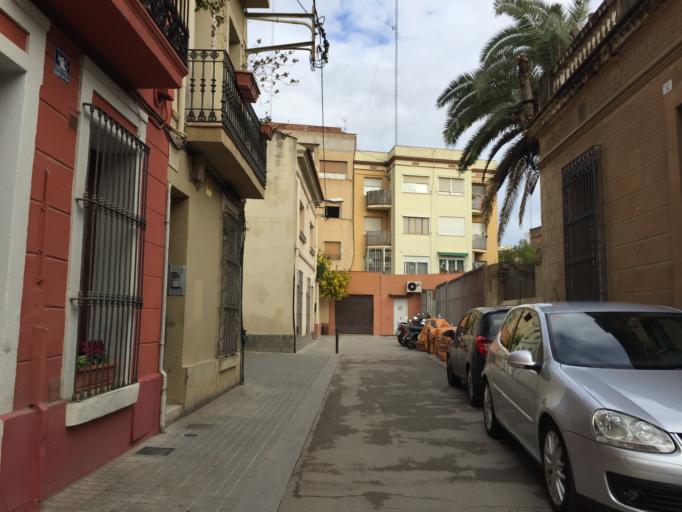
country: ES
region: Catalonia
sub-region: Provincia de Barcelona
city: Gracia
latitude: 41.4082
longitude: 2.1535
